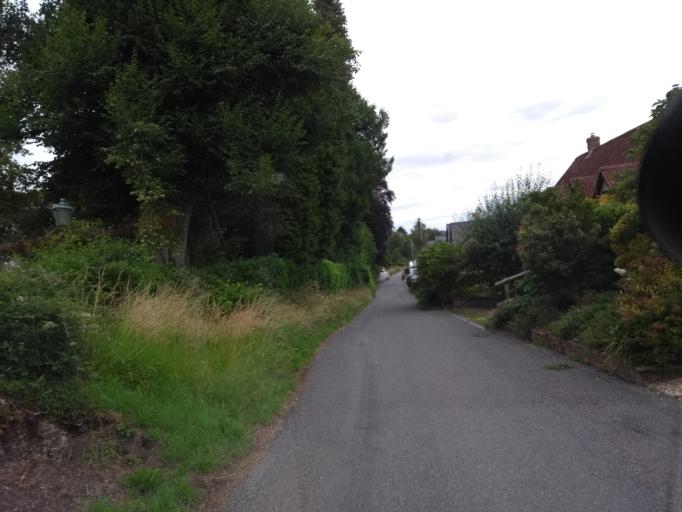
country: GB
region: England
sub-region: Somerset
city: Ilminster
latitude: 50.9351
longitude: -2.8835
